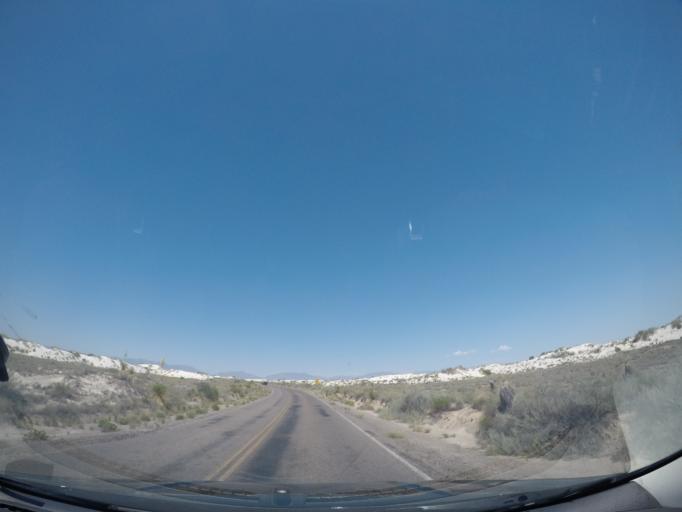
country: US
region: New Mexico
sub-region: Otero County
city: Holloman Air Force Base
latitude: 32.7974
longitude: -106.2231
